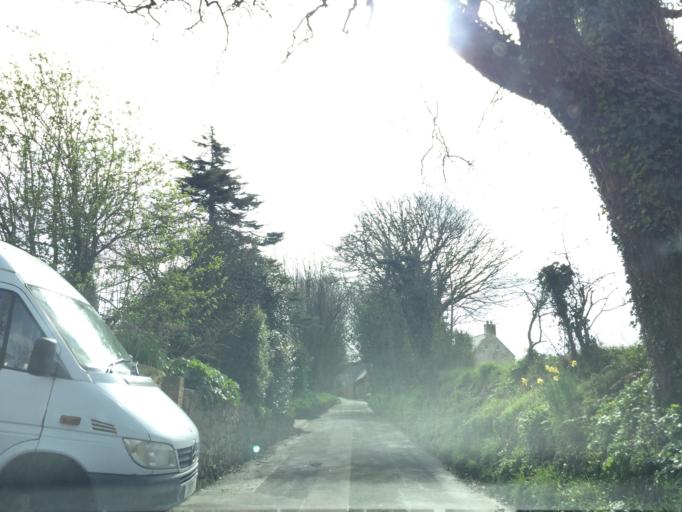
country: JE
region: St Helier
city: Saint Helier
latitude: 49.2022
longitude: -2.0672
